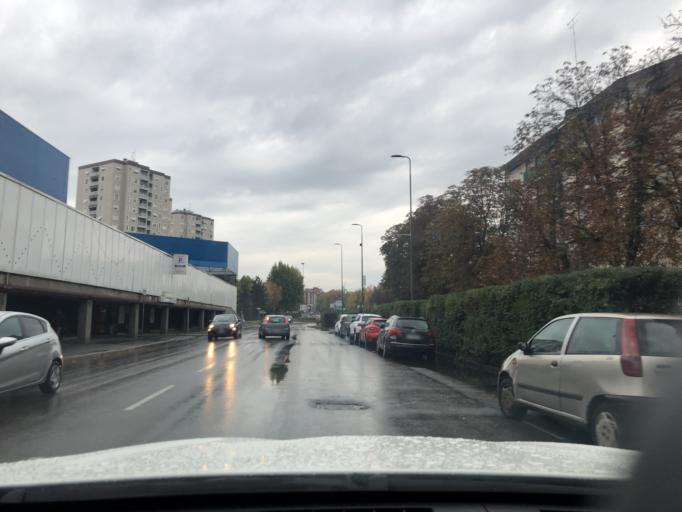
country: IT
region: Lombardy
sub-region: Citta metropolitana di Milano
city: Pero
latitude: 45.4974
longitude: 9.1134
